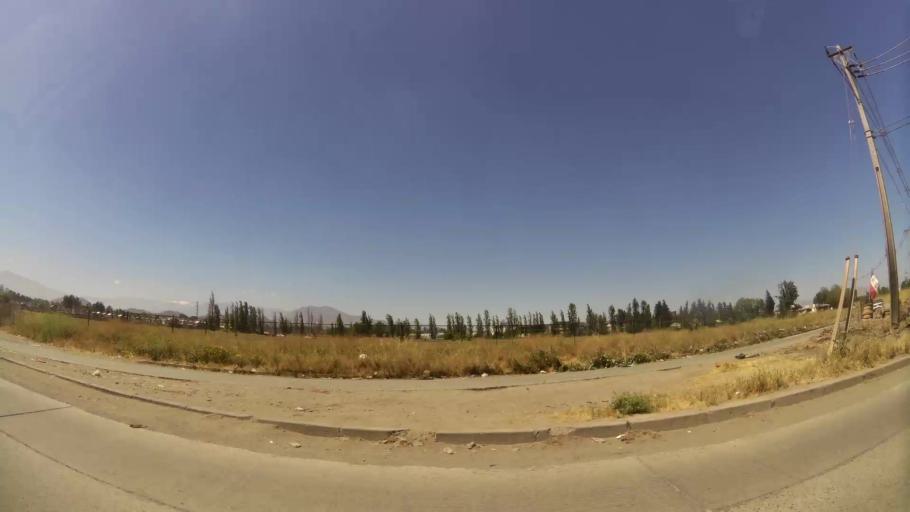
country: CL
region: Santiago Metropolitan
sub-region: Provincia de Maipo
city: San Bernardo
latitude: -33.6259
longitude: -70.7114
